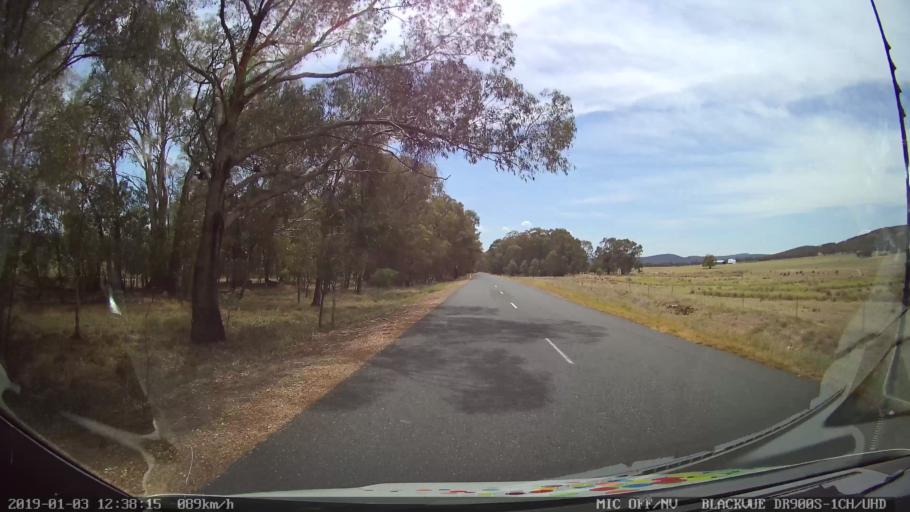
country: AU
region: New South Wales
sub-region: Weddin
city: Grenfell
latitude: -33.8349
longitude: 148.1932
